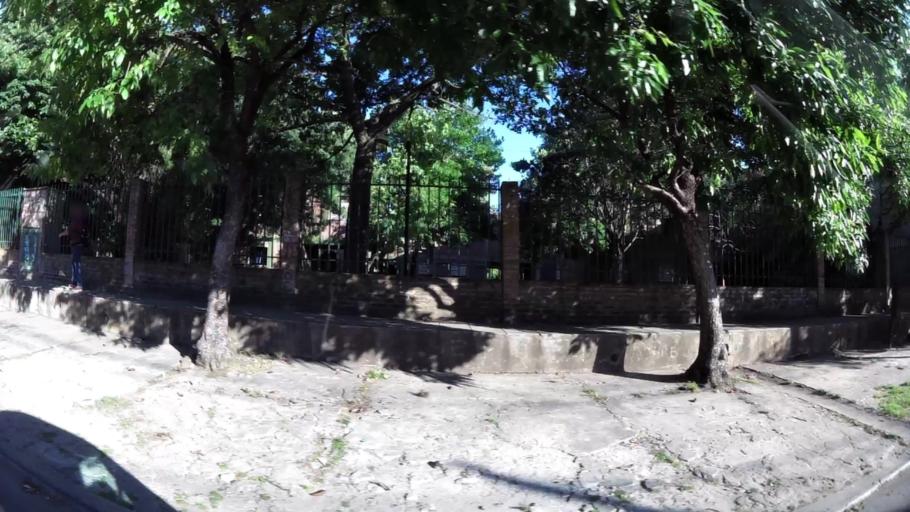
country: AR
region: Buenos Aires
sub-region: Partido de Moron
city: Moron
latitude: -34.6880
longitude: -58.6284
